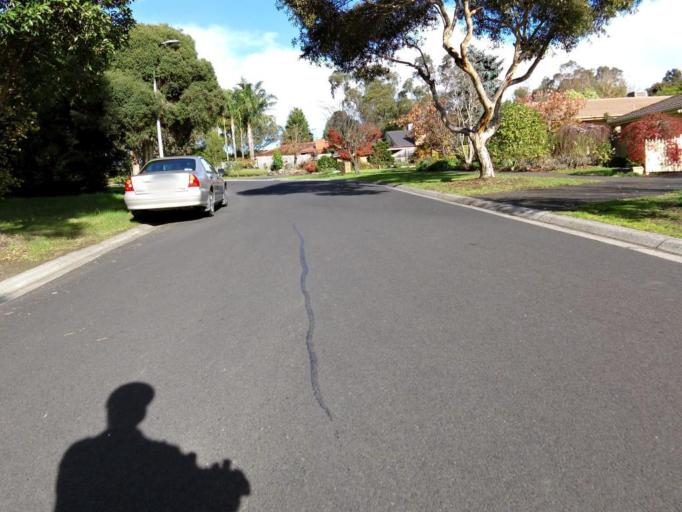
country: AU
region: Victoria
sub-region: Maroondah
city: Croydon Hills
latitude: -37.7713
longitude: 145.2637
